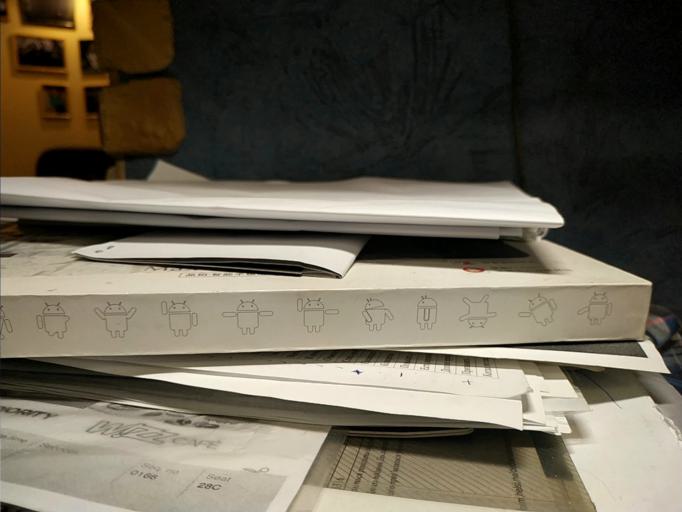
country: RU
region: Tverskaya
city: Zubtsov
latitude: 56.0832
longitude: 34.7853
